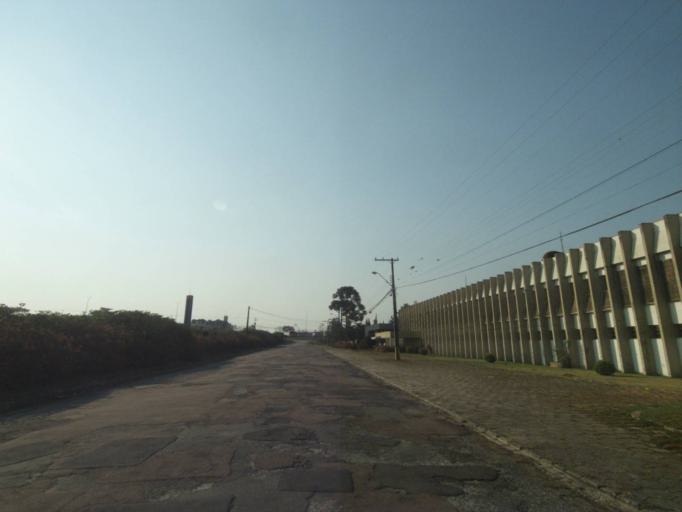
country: BR
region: Parana
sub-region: Curitiba
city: Curitiba
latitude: -25.4891
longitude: -49.2674
